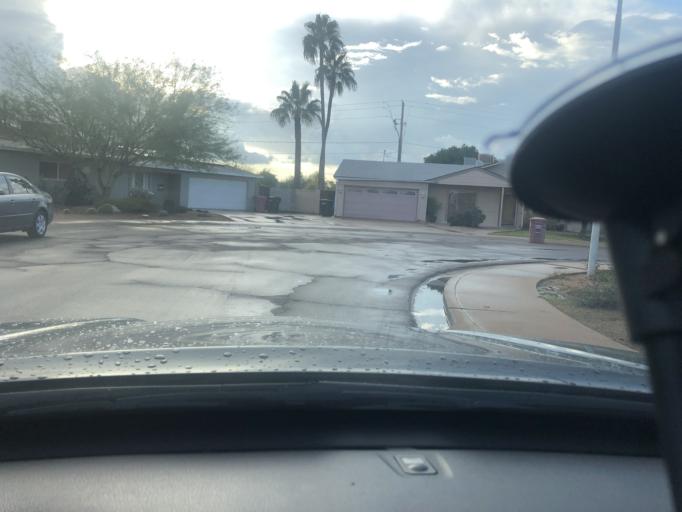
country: US
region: Arizona
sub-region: Maricopa County
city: Scottsdale
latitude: 33.4900
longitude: -111.8981
